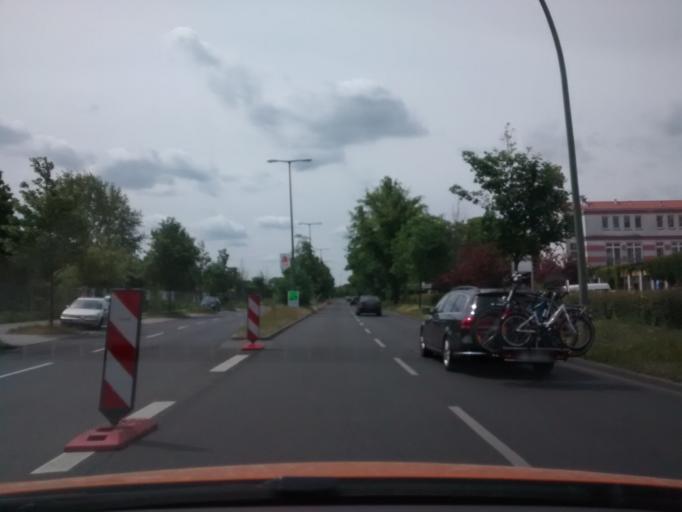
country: DE
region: Berlin
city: Marienfelde
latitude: 52.4079
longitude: 13.3583
